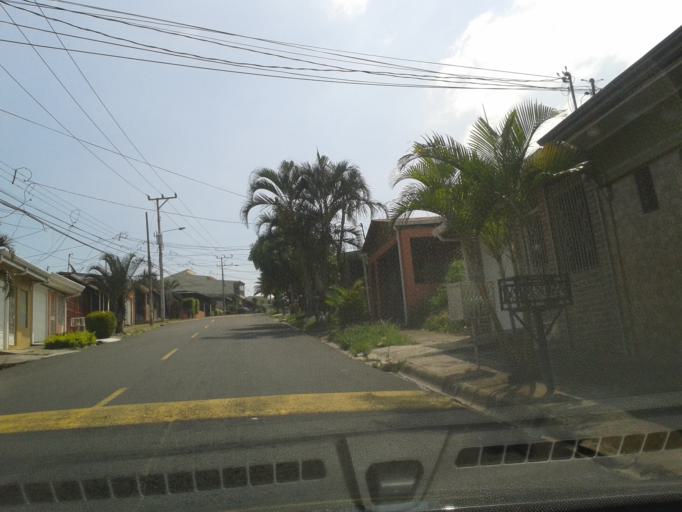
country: CR
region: Heredia
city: San Francisco
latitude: 9.9832
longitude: -84.1367
